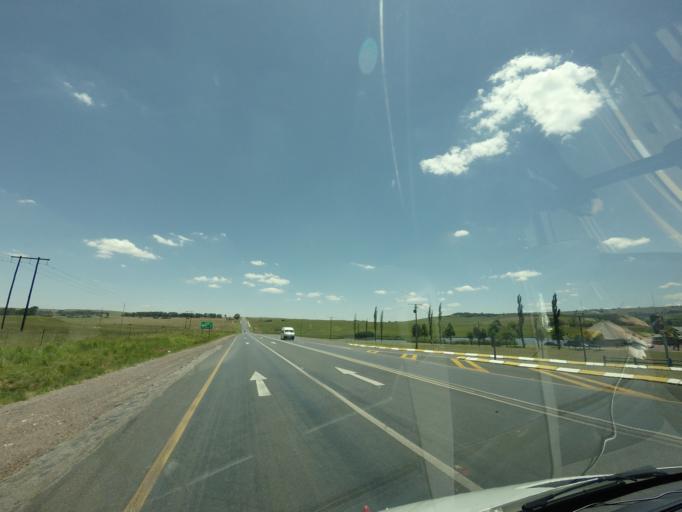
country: ZA
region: Mpumalanga
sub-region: Nkangala District Municipality
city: Belfast
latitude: -25.6895
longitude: 30.2129
